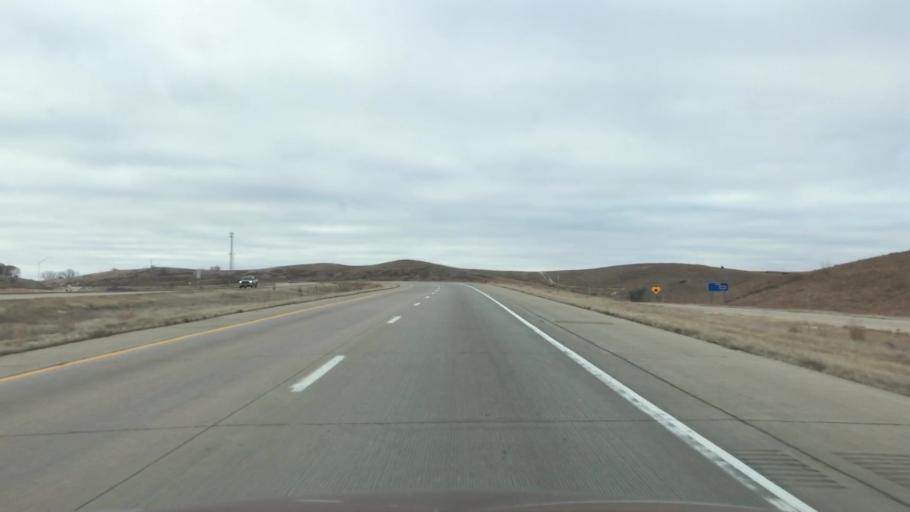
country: US
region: Iowa
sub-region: Woodbury County
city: Sioux City
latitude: 42.5223
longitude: -96.3395
